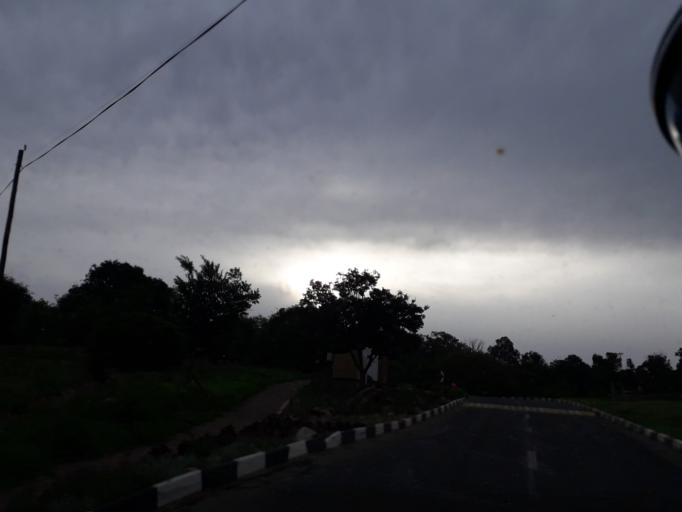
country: ZA
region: Gauteng
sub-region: City of Johannesburg Metropolitan Municipality
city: Johannesburg
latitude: -26.0843
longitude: 28.0122
